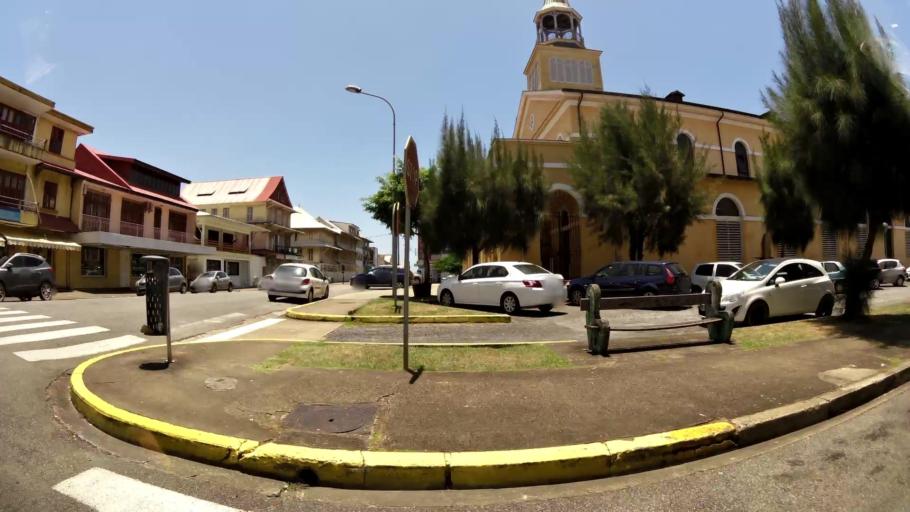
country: GF
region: Guyane
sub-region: Guyane
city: Cayenne
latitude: 4.9394
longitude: -52.3318
